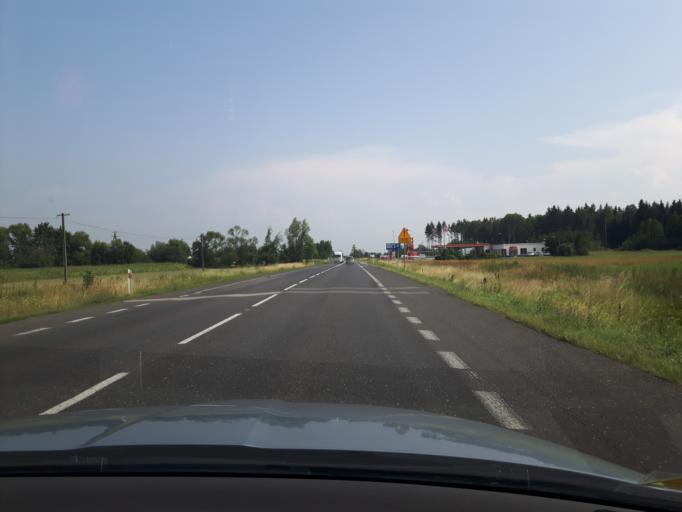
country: PL
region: Masovian Voivodeship
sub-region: Powiat plonski
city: Plonsk
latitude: 52.6997
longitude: 20.3411
